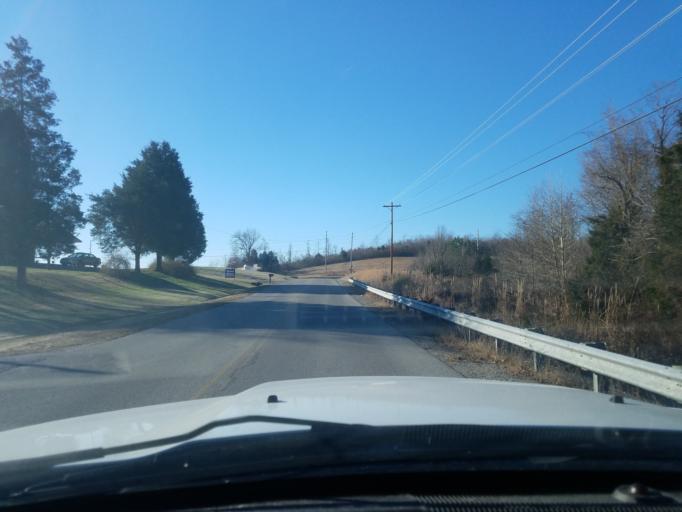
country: US
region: Kentucky
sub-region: Ohio County
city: Beaver Dam
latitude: 37.3662
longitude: -86.8380
